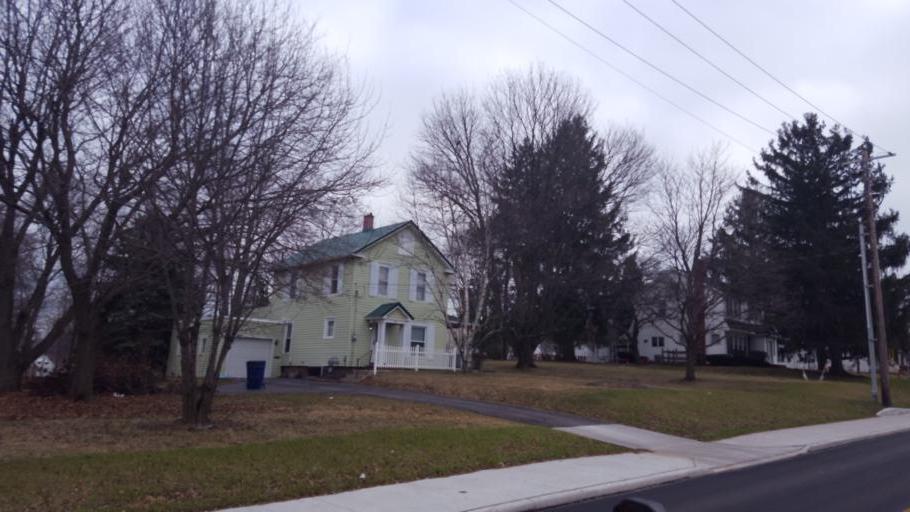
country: US
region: Ohio
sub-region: Richland County
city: Shelby
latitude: 40.8780
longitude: -82.6553
